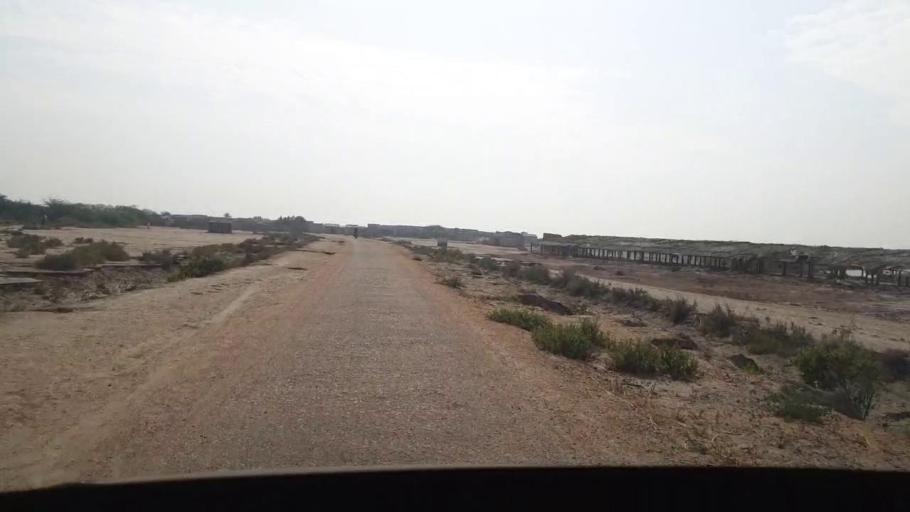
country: PK
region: Sindh
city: Chuhar Jamali
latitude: 24.2379
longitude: 67.9845
